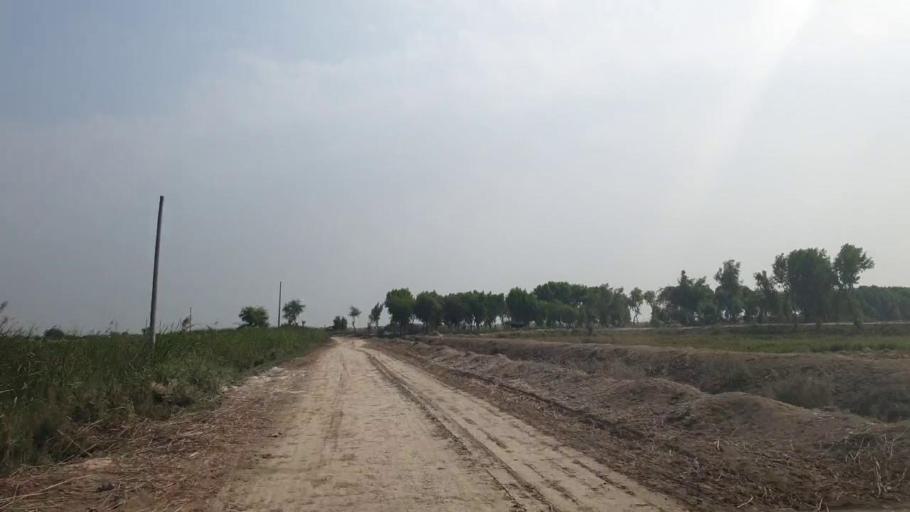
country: PK
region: Sindh
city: Badin
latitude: 24.7630
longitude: 68.7897
